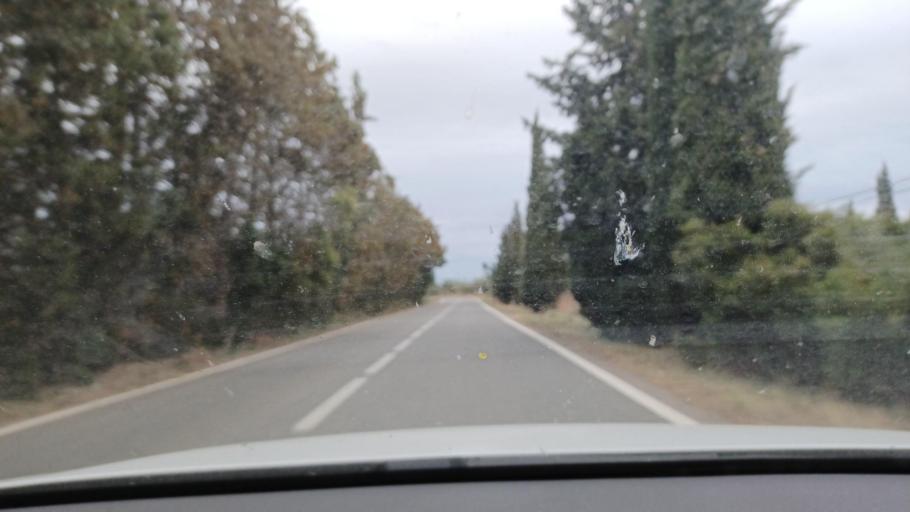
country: ES
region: Catalonia
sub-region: Provincia de Tarragona
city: Ulldecona
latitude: 40.6164
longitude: 0.3569
